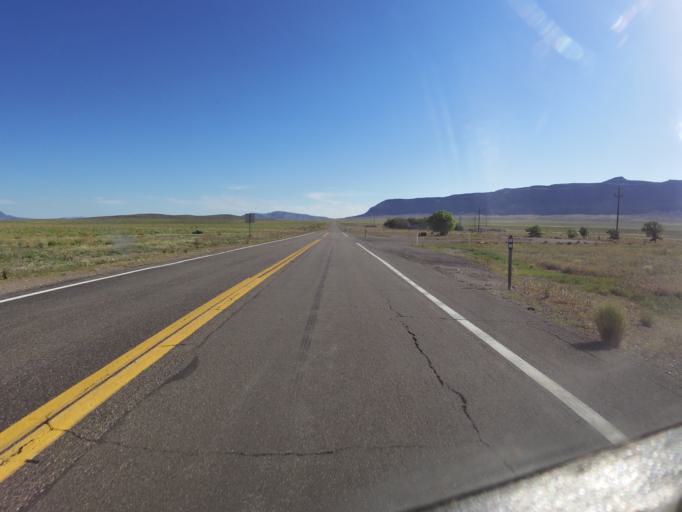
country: US
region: Nevada
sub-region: Nye County
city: Tonopah
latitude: 38.3687
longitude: -116.2294
